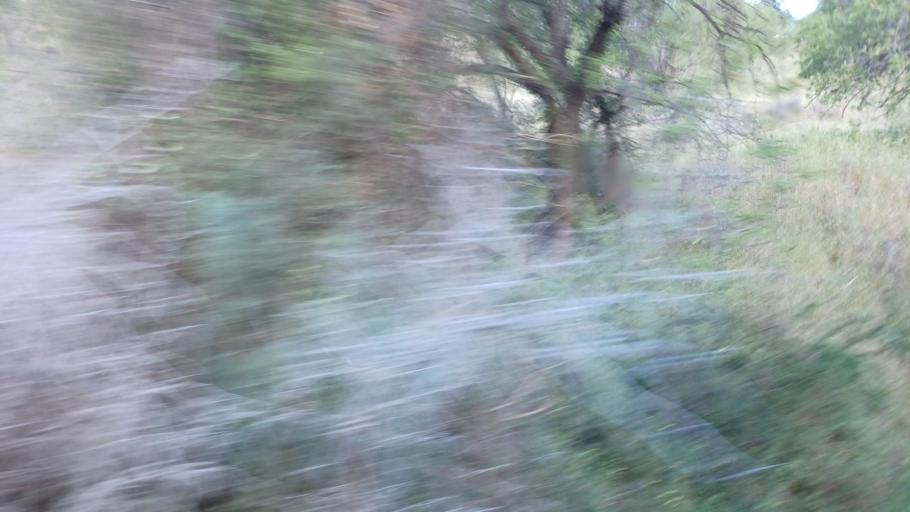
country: CY
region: Lefkosia
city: Peristerona
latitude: 35.0291
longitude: 33.0542
